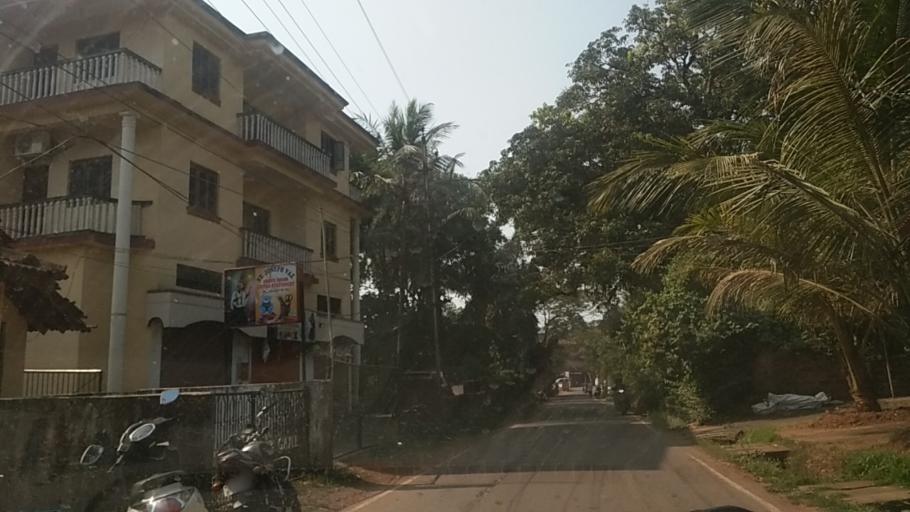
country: IN
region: Goa
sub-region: South Goa
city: Cortalim
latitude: 15.3975
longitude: 73.9118
